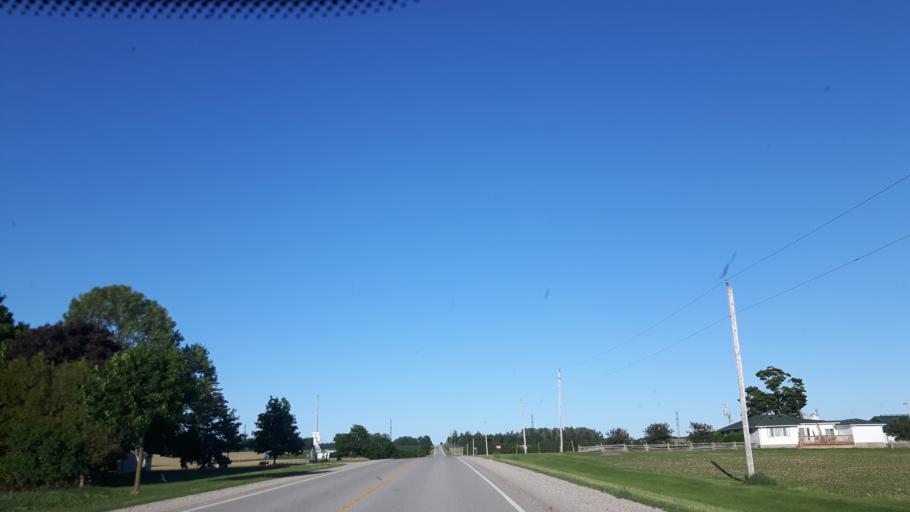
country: CA
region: Ontario
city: Goderich
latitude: 43.6427
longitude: -81.6525
